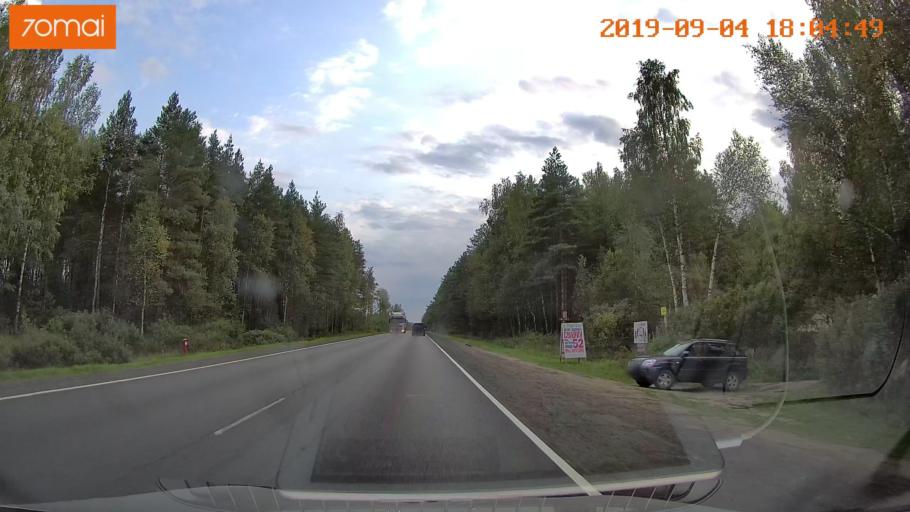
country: RU
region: Moskovskaya
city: Il'inskiy Pogost
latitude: 55.4480
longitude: 38.8342
